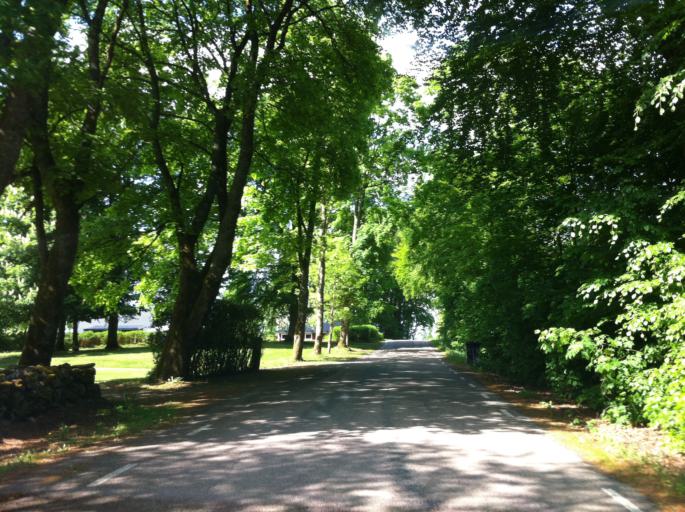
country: SE
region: Skane
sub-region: Svalovs Kommun
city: Kagerod
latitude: 56.0297
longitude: 13.1582
